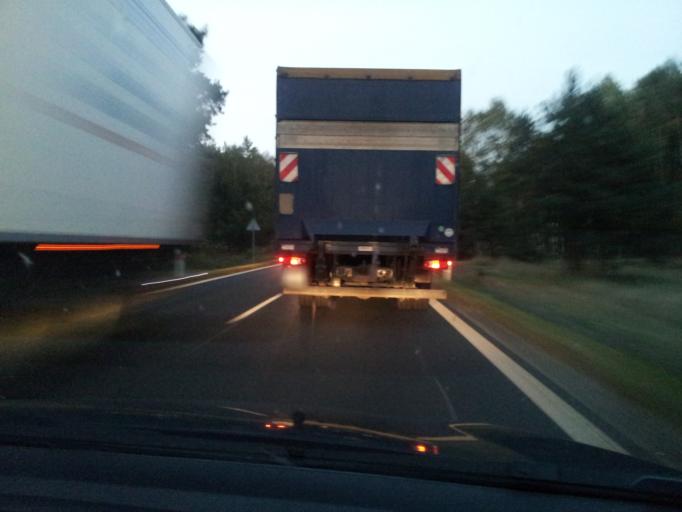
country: PL
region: Kujawsko-Pomorskie
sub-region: Powiat torunski
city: Wielka Nieszawka
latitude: 52.9570
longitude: 18.5328
